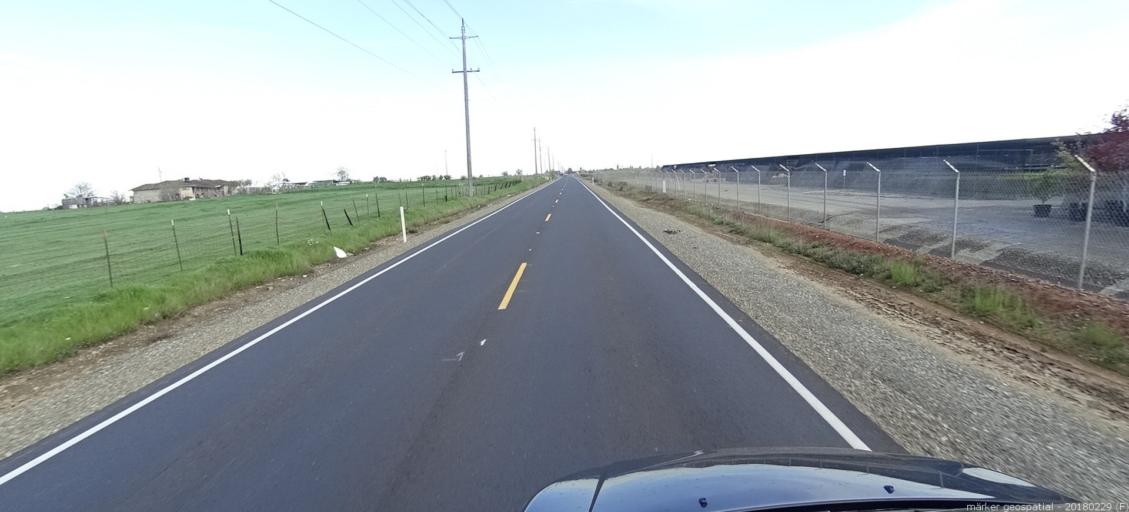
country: US
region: California
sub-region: Sacramento County
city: Vineyard
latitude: 38.4921
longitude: -121.2977
